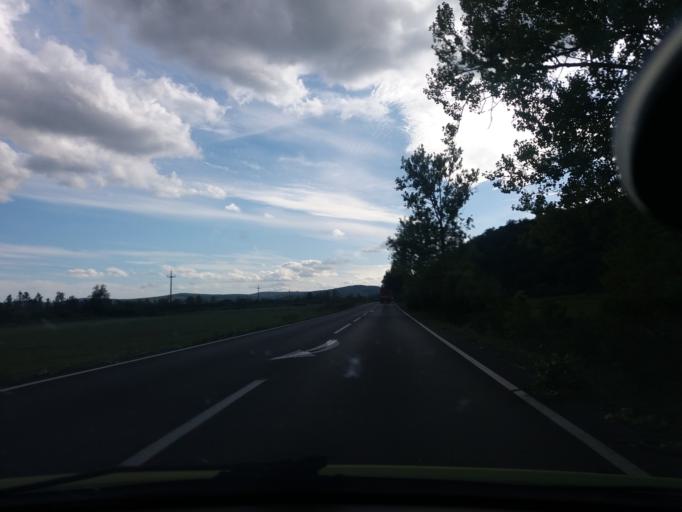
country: RO
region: Arad
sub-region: Comuna Ususau
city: Ususau
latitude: 46.1002
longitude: 21.8146
